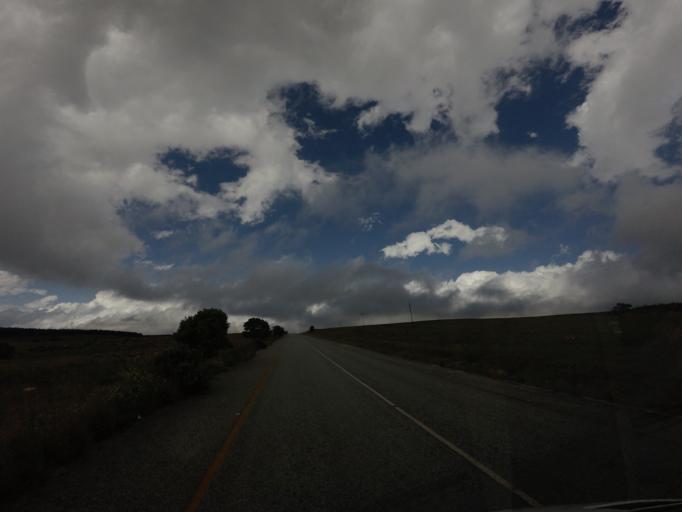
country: ZA
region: Mpumalanga
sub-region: Ehlanzeni District
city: Graksop
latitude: -24.8600
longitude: 30.8662
